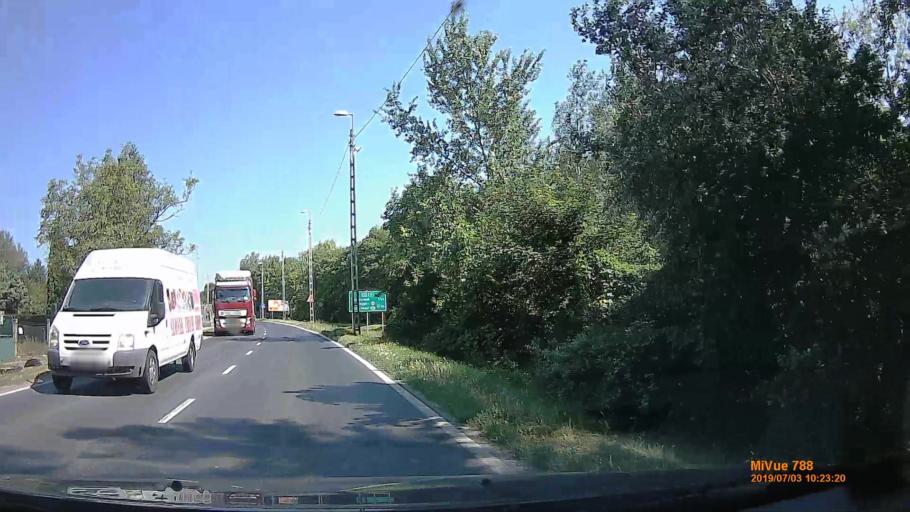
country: HU
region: Gyor-Moson-Sopron
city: Gyor
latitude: 47.7134
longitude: 17.6366
